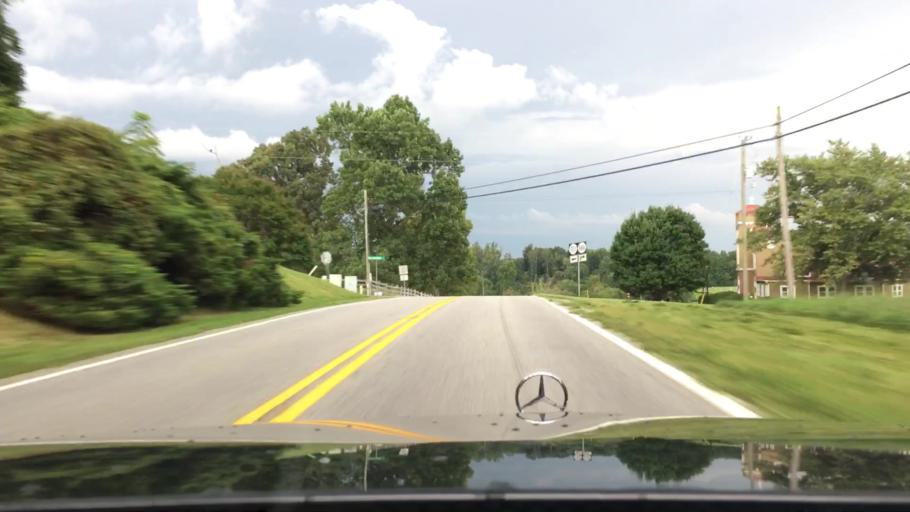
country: US
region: Virginia
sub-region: Nelson County
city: Lovingston
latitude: 37.7847
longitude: -78.9780
